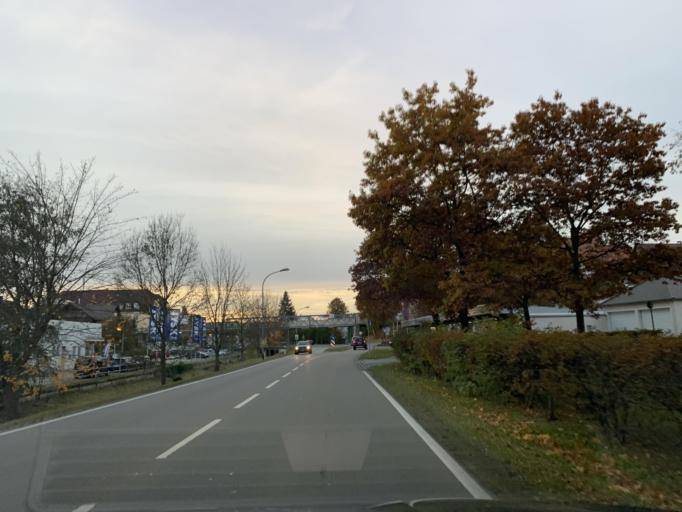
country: DE
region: Bavaria
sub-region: Upper Palatinate
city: Neunburg vorm Wald
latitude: 49.3469
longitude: 12.3853
